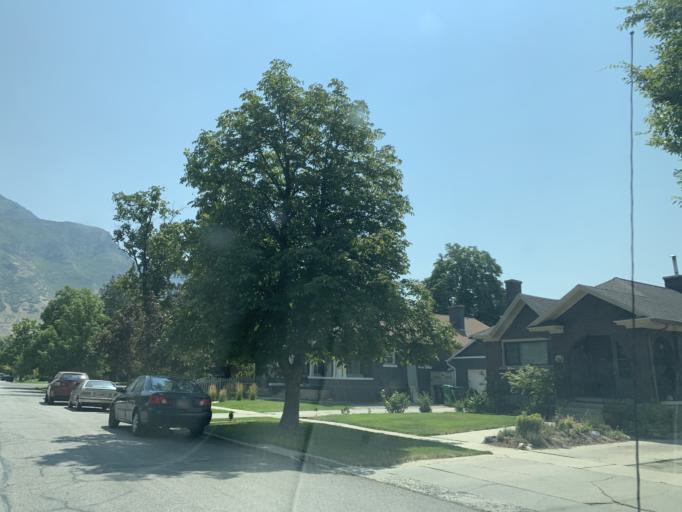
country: US
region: Utah
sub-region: Utah County
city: Provo
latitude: 40.2364
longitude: -111.6546
